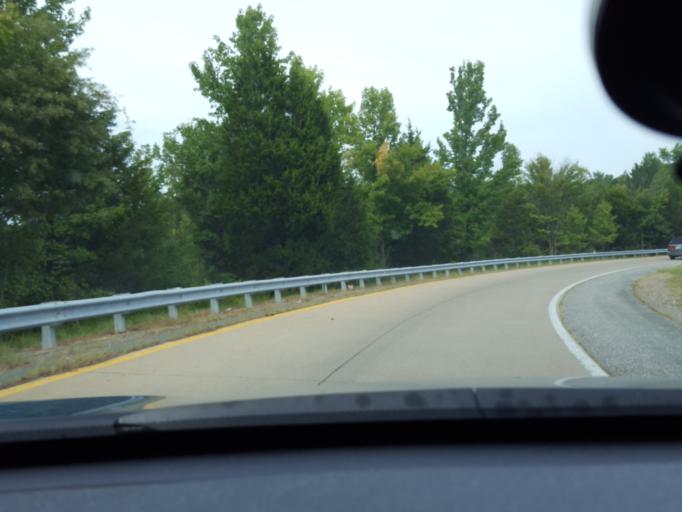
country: US
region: Virginia
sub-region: Henrico County
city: Chamberlayne
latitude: 37.6457
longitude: -77.4166
